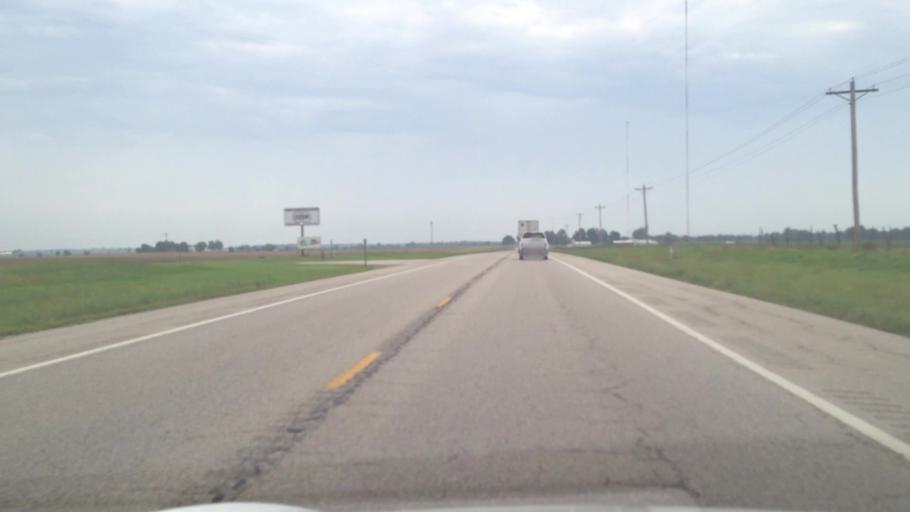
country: US
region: Missouri
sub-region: Jasper County
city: Carl Junction
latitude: 37.2320
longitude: -94.7050
